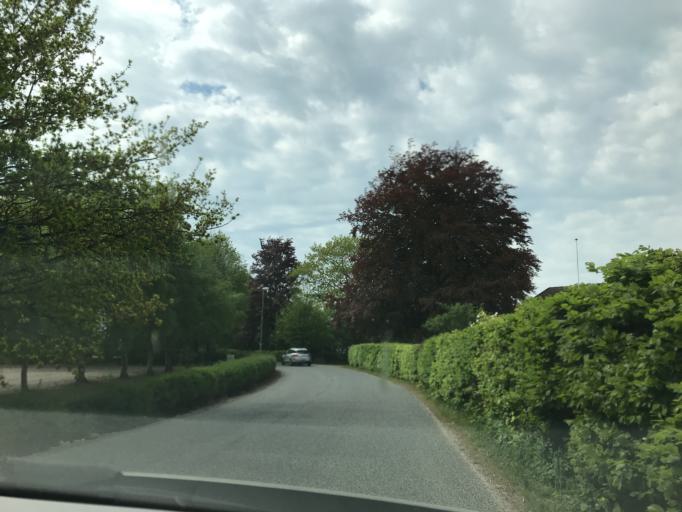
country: DK
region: South Denmark
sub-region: Assens Kommune
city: Assens
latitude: 55.3279
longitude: 9.9226
